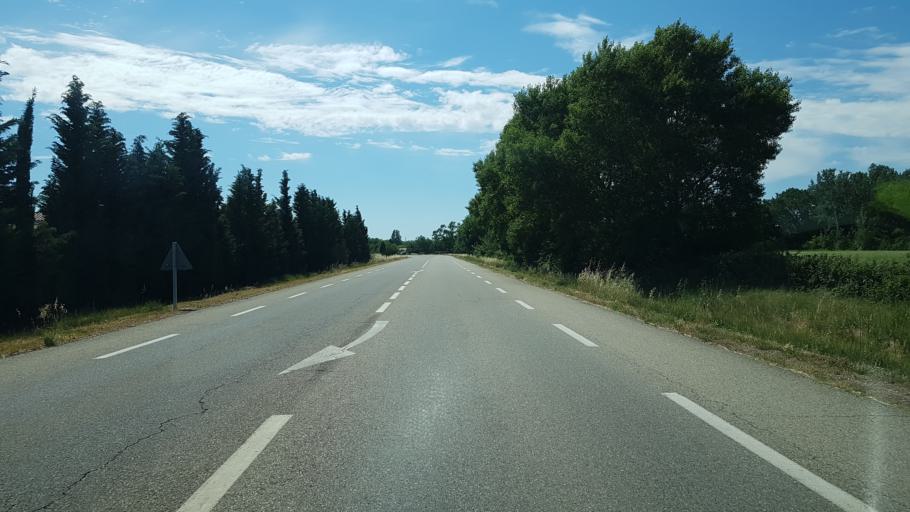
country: FR
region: Provence-Alpes-Cote d'Azur
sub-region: Departement des Bouches-du-Rhone
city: Saint-Martin-de-Crau
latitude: 43.6465
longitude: 4.8147
